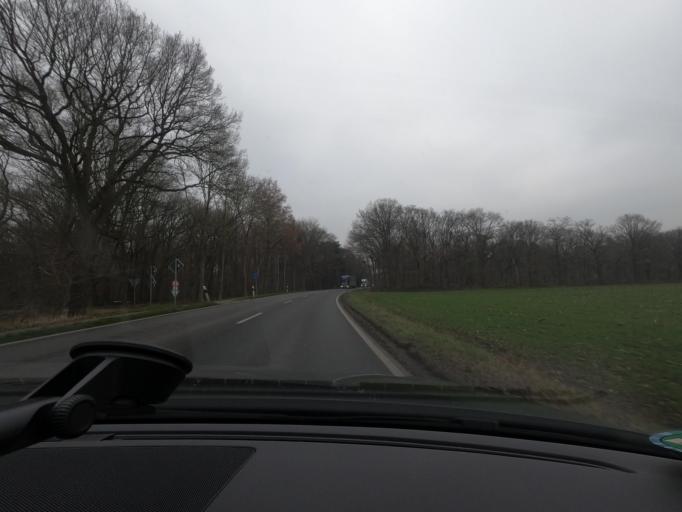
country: DE
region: North Rhine-Westphalia
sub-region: Regierungsbezirk Dusseldorf
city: Nettetal
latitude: 51.3468
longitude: 6.2317
